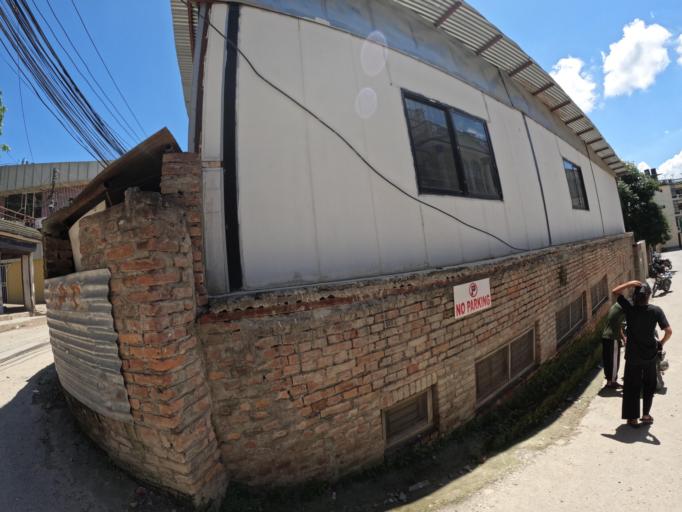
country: NP
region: Central Region
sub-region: Bagmati Zone
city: Kathmandu
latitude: 27.7390
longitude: 85.3239
